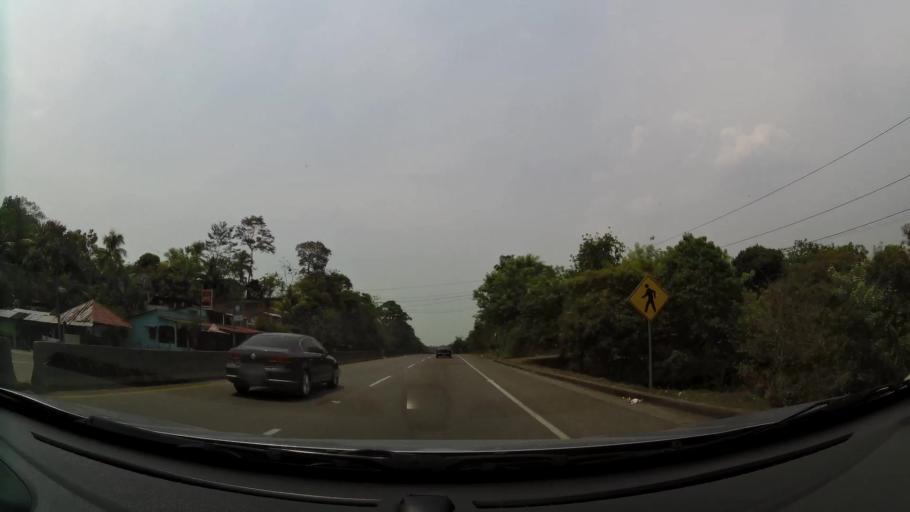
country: HN
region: Cortes
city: Oropendolas
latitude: 14.9926
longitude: -87.9311
